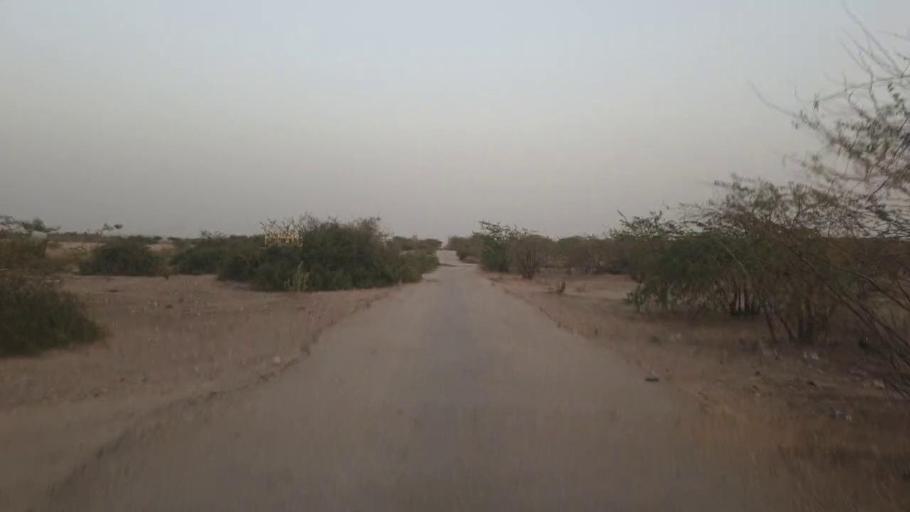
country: PK
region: Sindh
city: Chor
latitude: 25.5155
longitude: 69.8101
